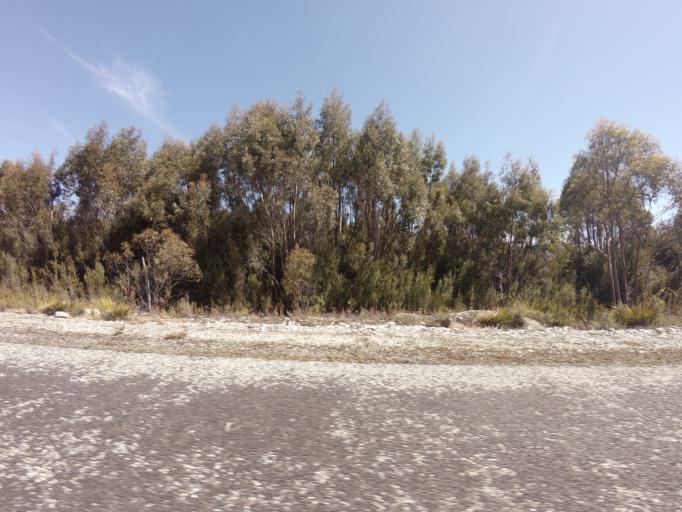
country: AU
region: Tasmania
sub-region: West Coast
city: Queenstown
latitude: -42.8001
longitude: 146.0914
